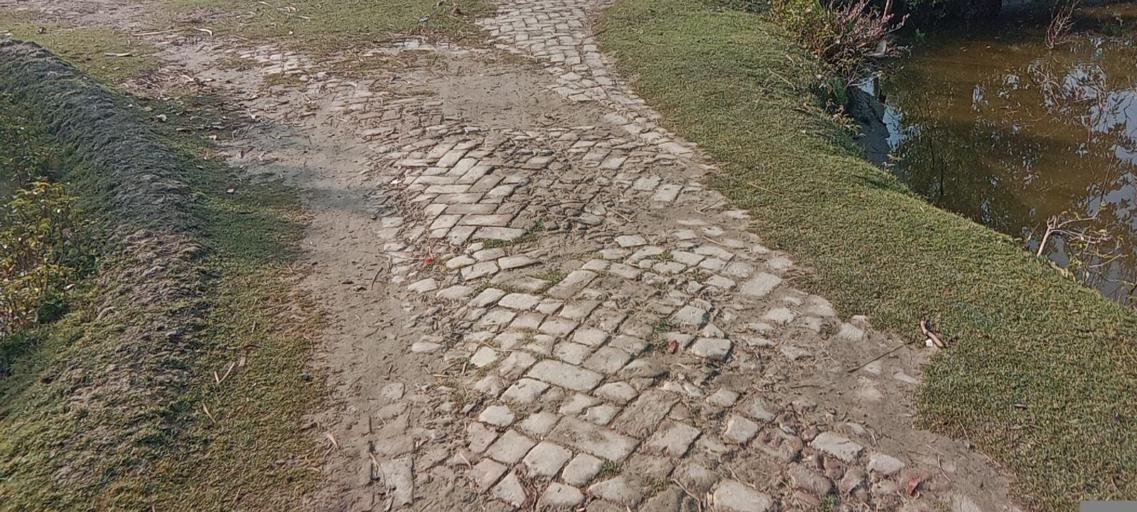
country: BD
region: Khulna
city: Phultala
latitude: 22.6119
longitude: 89.5835
